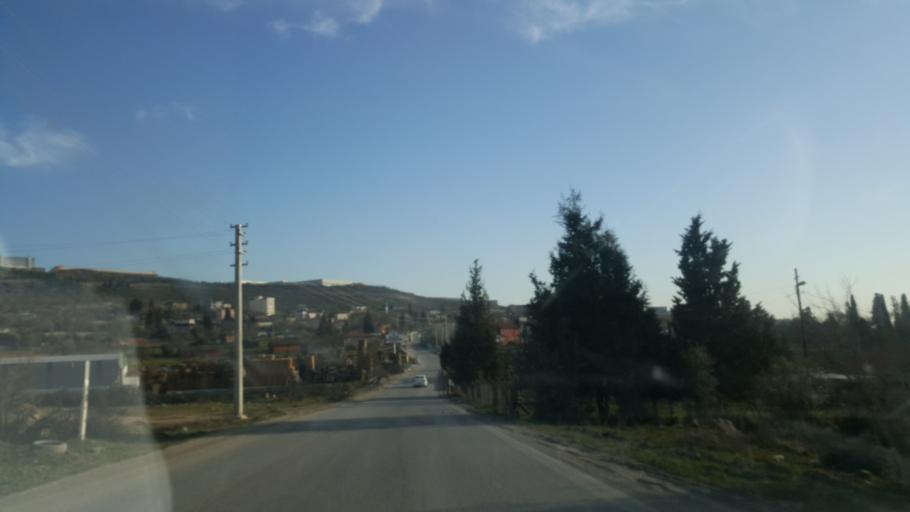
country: TR
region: Kocaeli
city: Tavsanli
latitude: 40.8513
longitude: 29.5552
